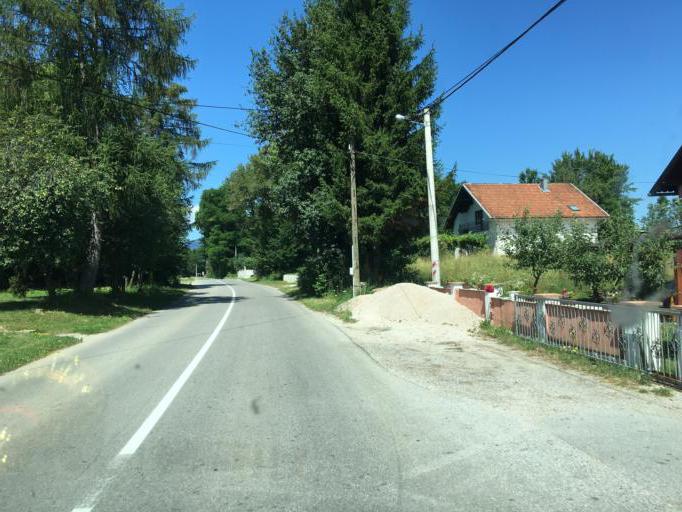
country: HR
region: Licko-Senjska
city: Gospic
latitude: 44.5556
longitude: 15.3410
